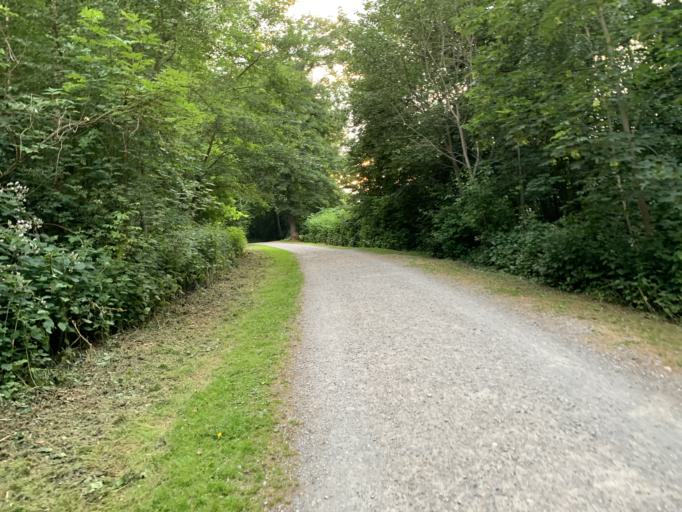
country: DE
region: North Rhine-Westphalia
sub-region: Regierungsbezirk Dusseldorf
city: Essen
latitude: 51.4208
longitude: 7.0090
